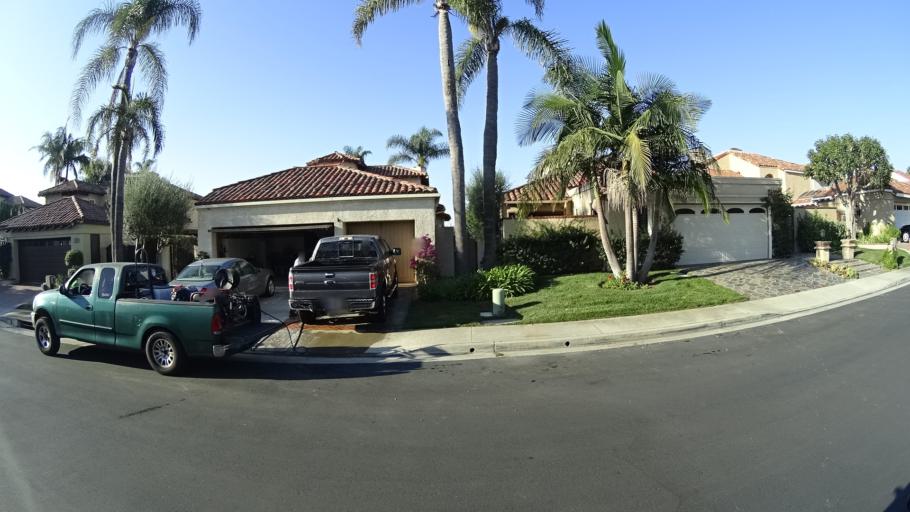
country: US
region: California
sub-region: Orange County
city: San Clemente
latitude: 33.4196
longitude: -117.5915
